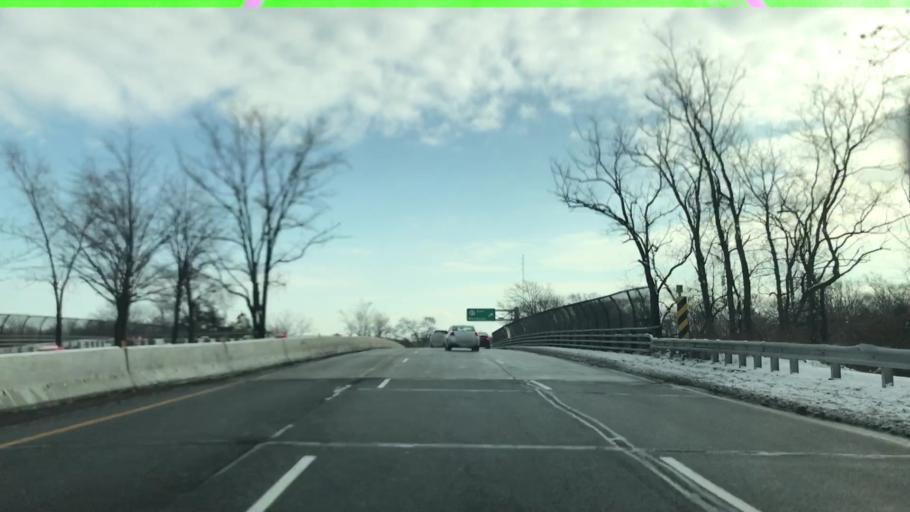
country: US
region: New York
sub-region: Suffolk County
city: North Lindenhurst
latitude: 40.7109
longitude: -73.3681
